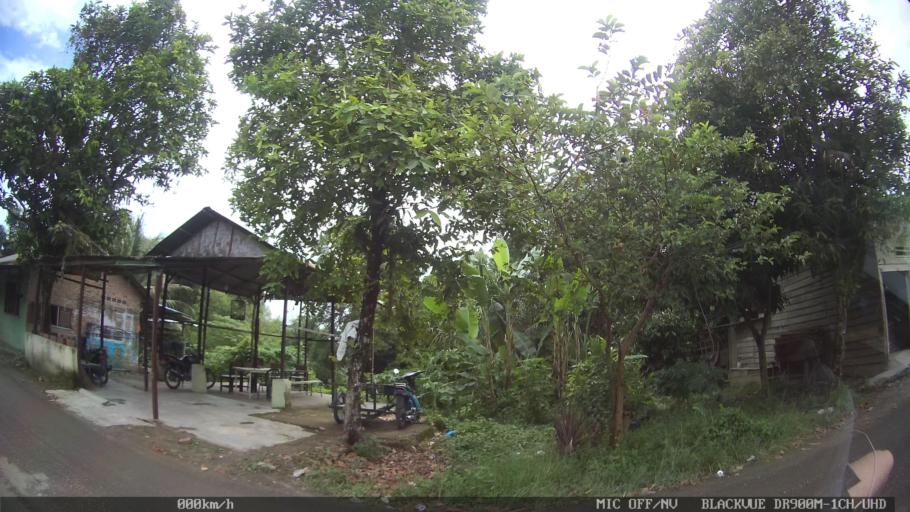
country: ID
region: North Sumatra
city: Sunggal
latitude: 3.6406
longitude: 98.5926
